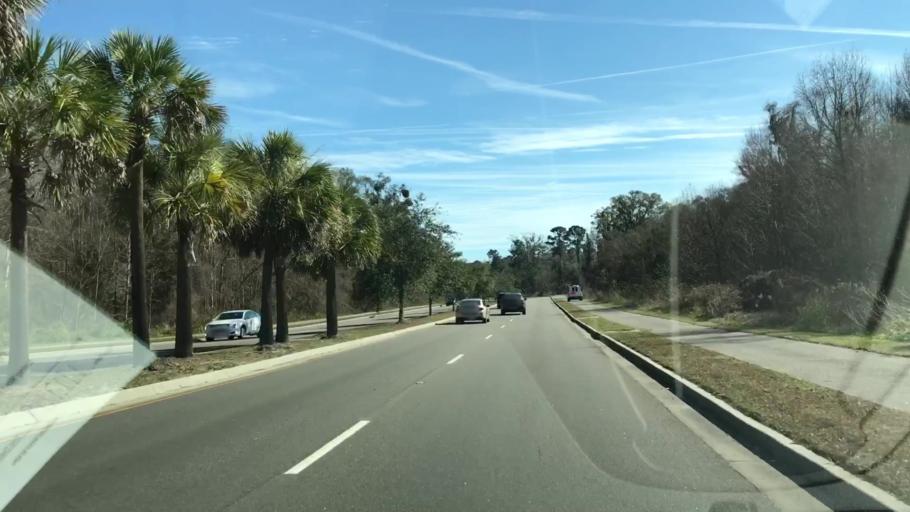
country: US
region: South Carolina
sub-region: Beaufort County
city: Bluffton
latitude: 32.2640
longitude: -80.8783
